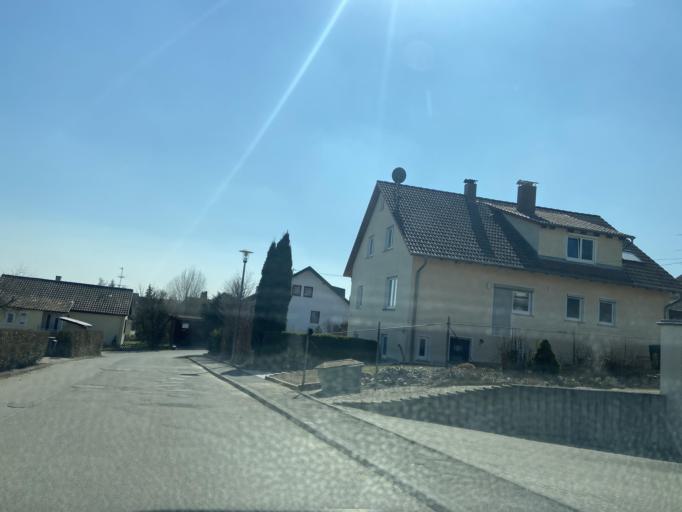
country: DE
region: Baden-Wuerttemberg
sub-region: Tuebingen Region
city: Inzigkofen
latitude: 48.0732
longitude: 9.1727
